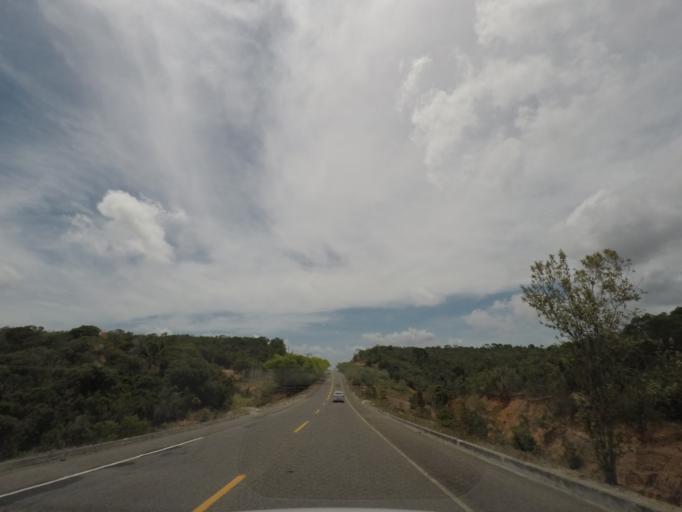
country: BR
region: Bahia
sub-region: Conde
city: Conde
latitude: -11.9159
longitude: -37.6615
